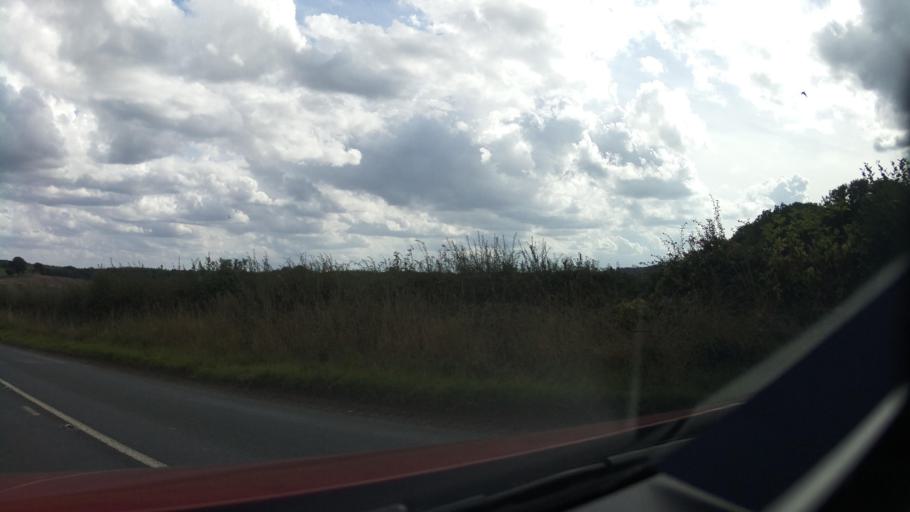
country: GB
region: England
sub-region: North Yorkshire
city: Bedale
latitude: 54.2213
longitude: -1.6372
